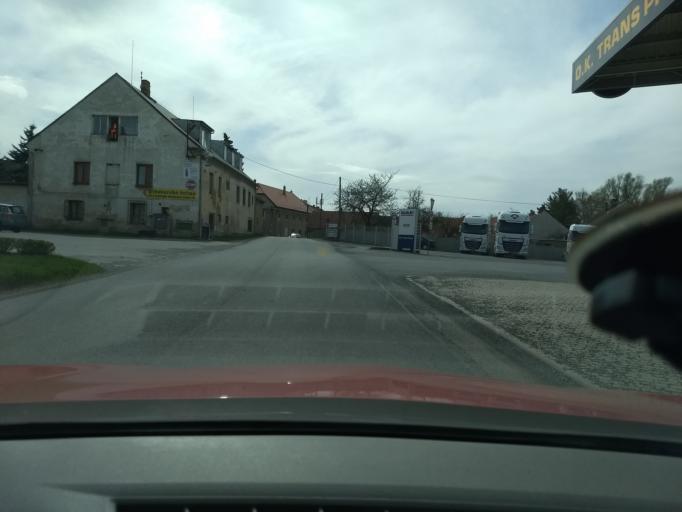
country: CZ
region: Central Bohemia
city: Rudna
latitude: 50.0630
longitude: 14.2330
